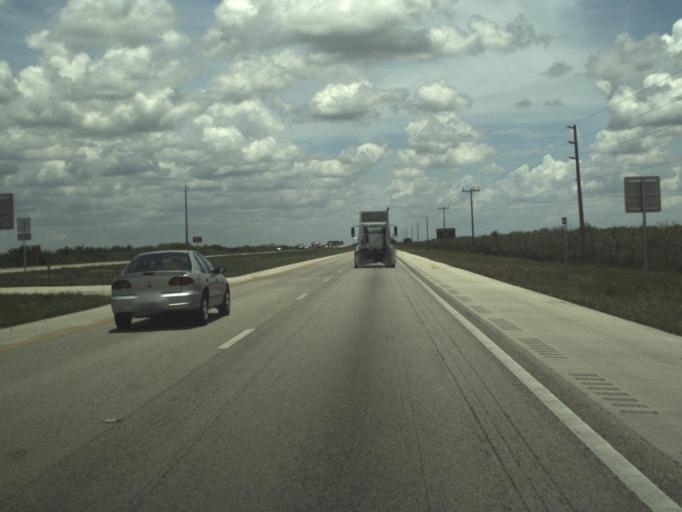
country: US
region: Florida
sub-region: Broward County
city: Weston
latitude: 26.1528
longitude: -80.7417
